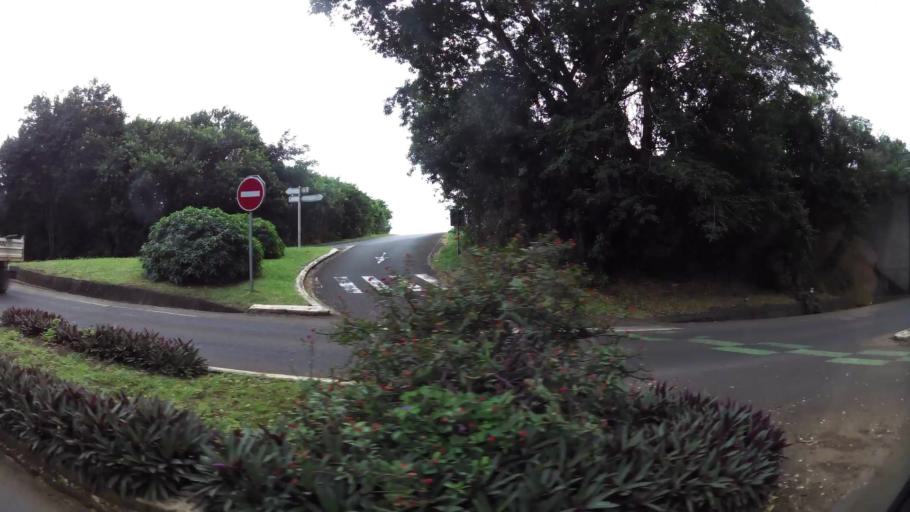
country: RE
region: Reunion
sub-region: Reunion
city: Sainte-Marie
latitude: -20.8966
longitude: 55.5606
